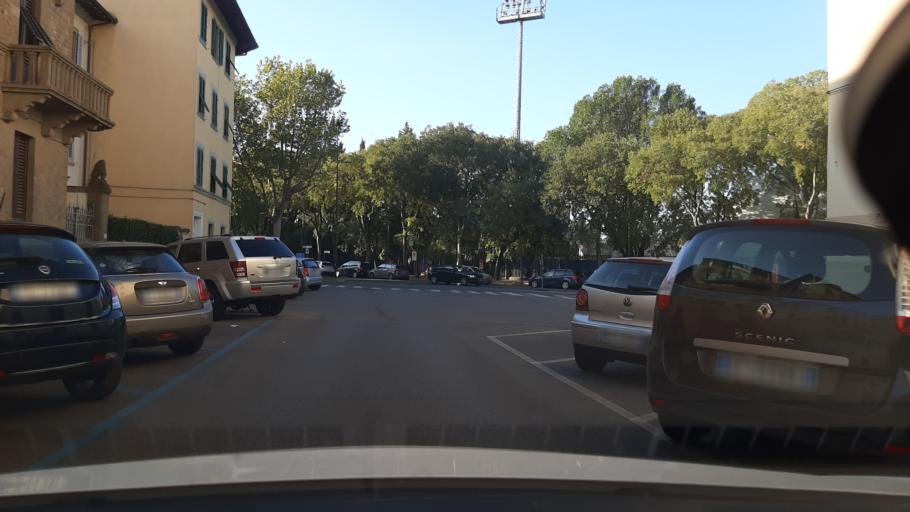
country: IT
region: Tuscany
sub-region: Province of Florence
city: Fiesole
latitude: 43.7804
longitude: 11.2886
